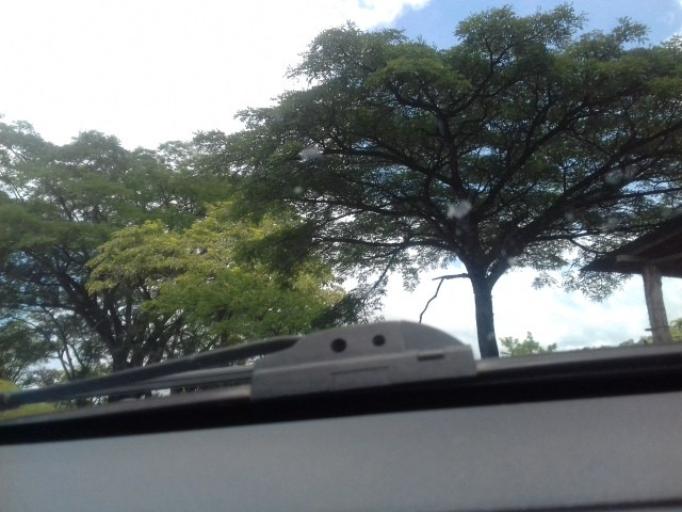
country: NI
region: Matagalpa
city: Matiguas
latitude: 13.0216
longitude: -85.4060
